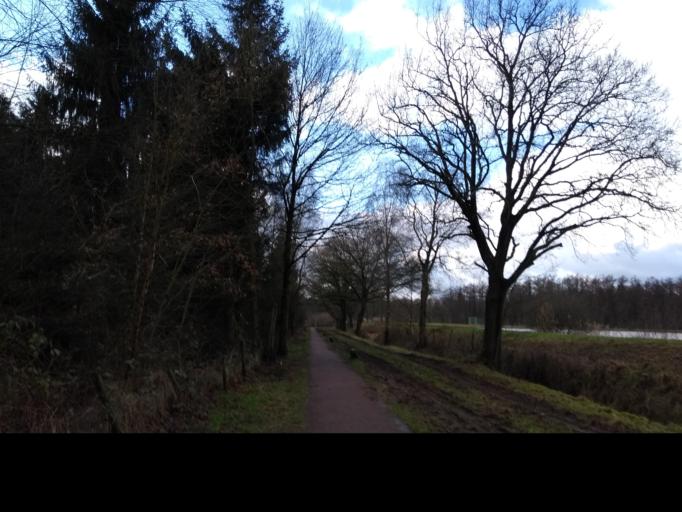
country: NL
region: Overijssel
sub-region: Gemeente Enschede
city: Enschede
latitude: 52.2486
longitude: 6.8689
